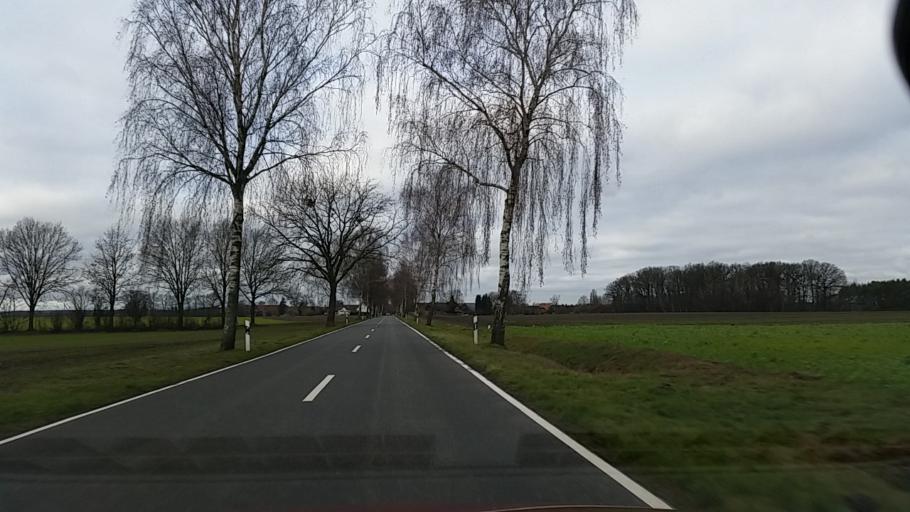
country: DE
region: Lower Saxony
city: Wittingen
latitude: 52.7638
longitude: 10.6973
